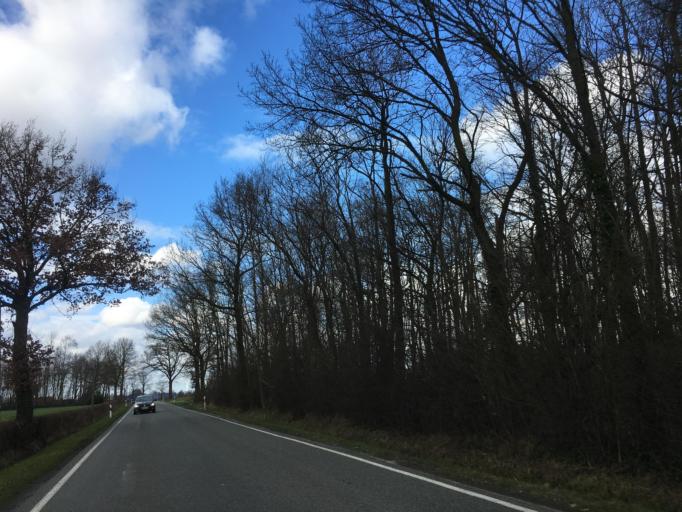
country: DE
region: North Rhine-Westphalia
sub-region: Regierungsbezirk Munster
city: Horstmar
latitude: 52.1010
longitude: 7.3189
